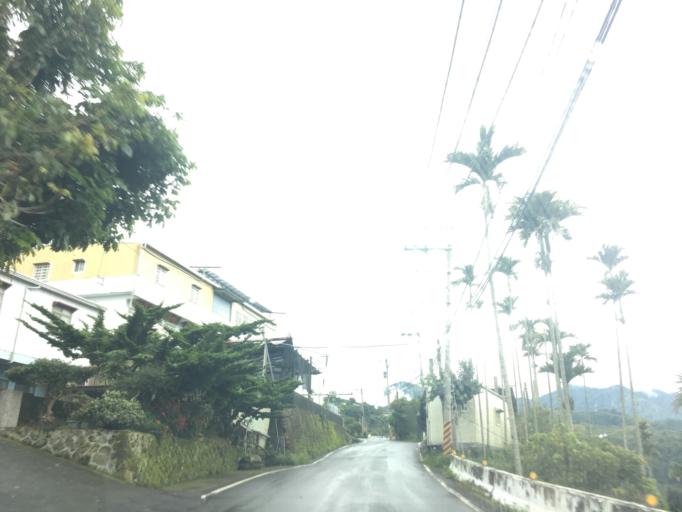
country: TW
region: Taiwan
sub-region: Yunlin
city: Douliu
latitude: 23.5618
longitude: 120.6584
